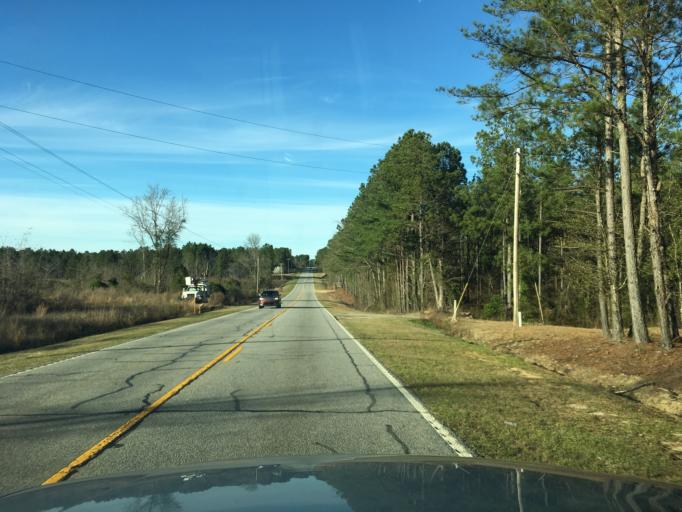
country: US
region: South Carolina
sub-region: Edgefield County
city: Johnston
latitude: 33.7539
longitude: -81.6431
